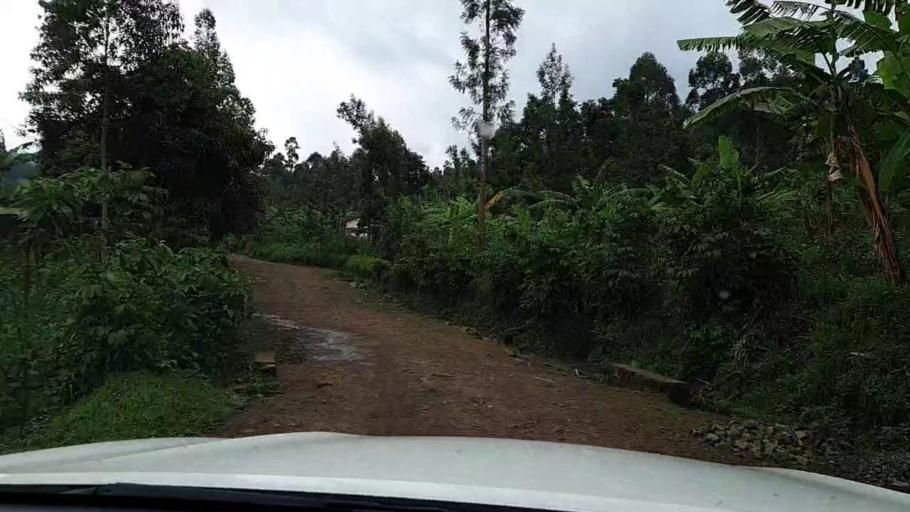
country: RW
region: Western Province
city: Cyangugu
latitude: -2.5423
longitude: 29.0390
